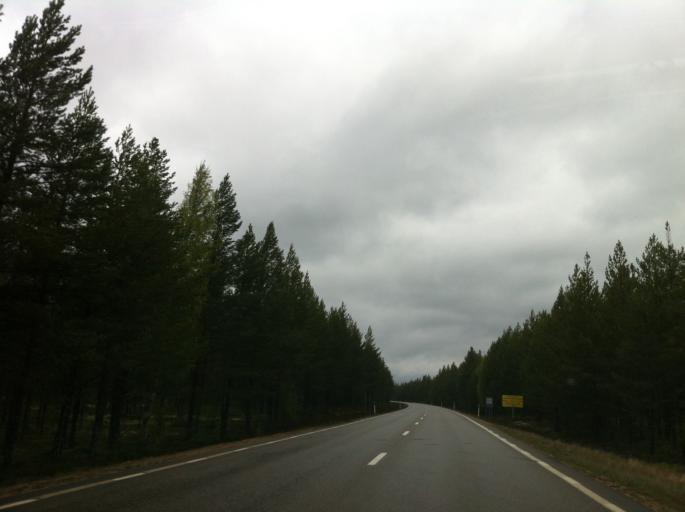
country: SE
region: Jaemtland
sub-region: Harjedalens Kommun
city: Sveg
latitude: 62.0567
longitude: 14.2991
